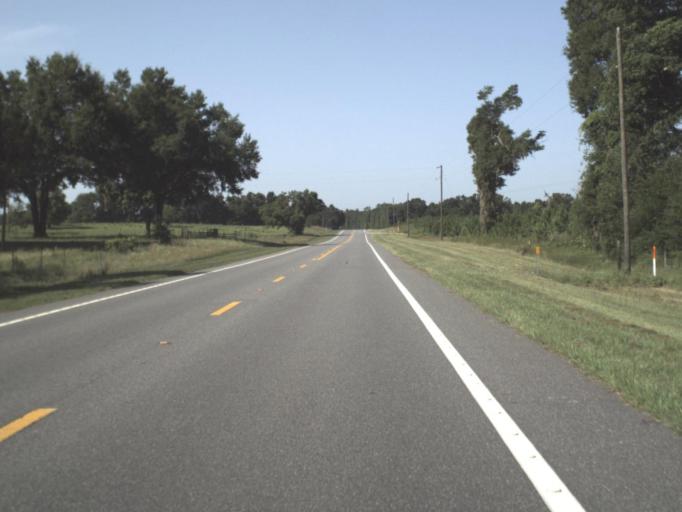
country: US
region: Florida
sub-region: Alachua County
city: High Springs
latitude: 29.8928
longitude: -82.7289
